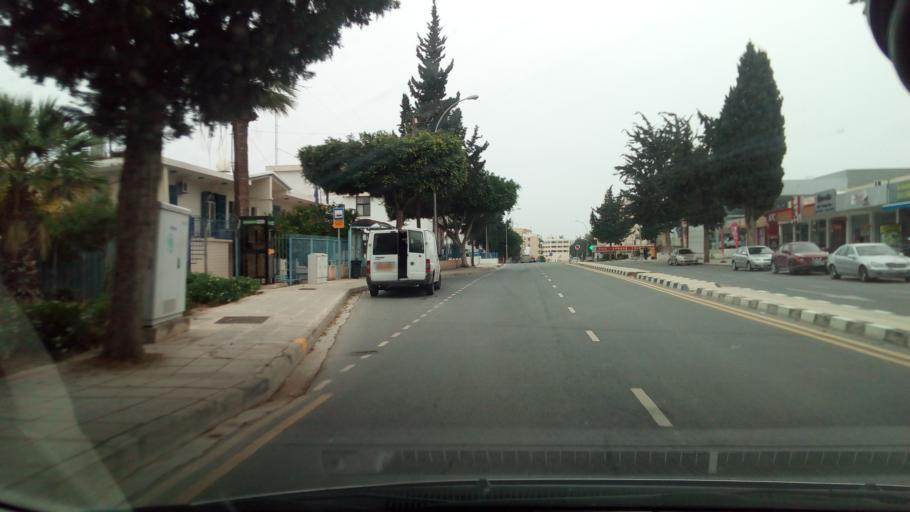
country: CY
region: Pafos
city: Paphos
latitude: 34.7691
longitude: 32.4364
